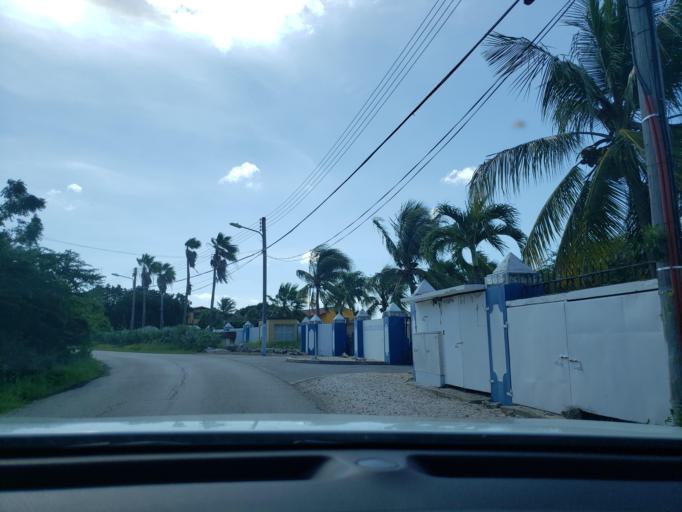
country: CW
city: Dorp Soto
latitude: 12.3640
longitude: -69.1547
